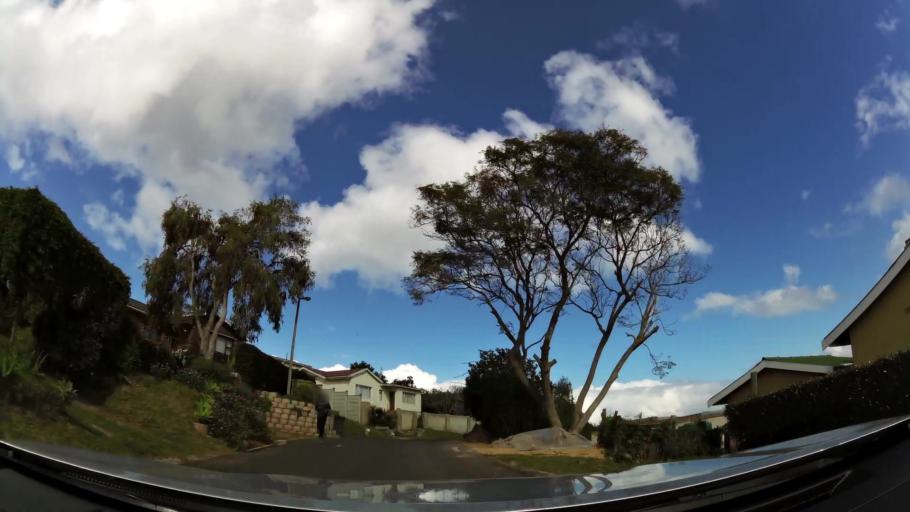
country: ZA
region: Western Cape
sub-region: Eden District Municipality
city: Knysna
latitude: -34.0497
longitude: 23.0843
